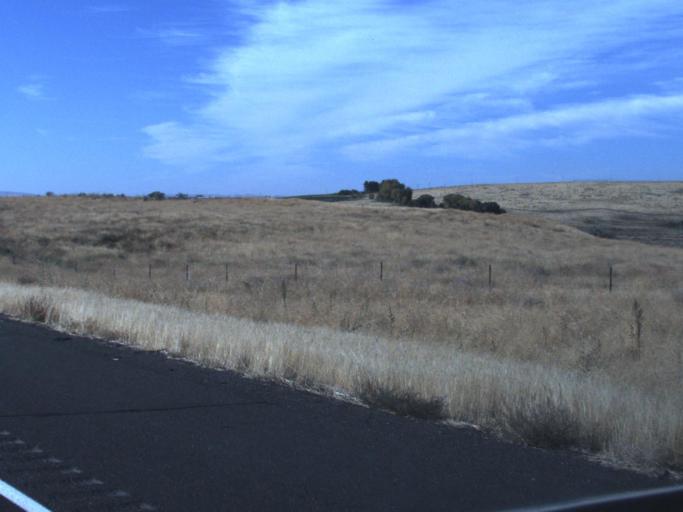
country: US
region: Washington
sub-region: Franklin County
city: Pasco
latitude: 46.4069
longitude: -119.0521
